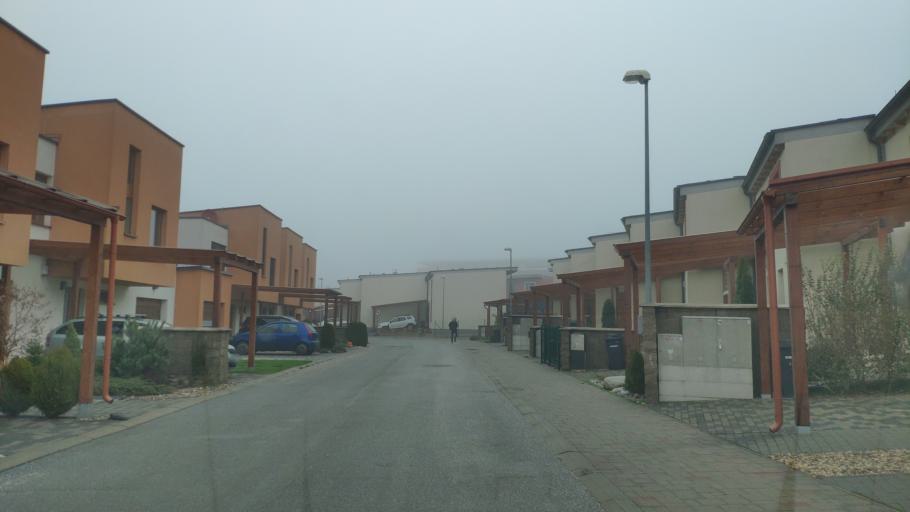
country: SK
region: Kosicky
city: Kosice
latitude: 48.7205
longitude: 21.2937
